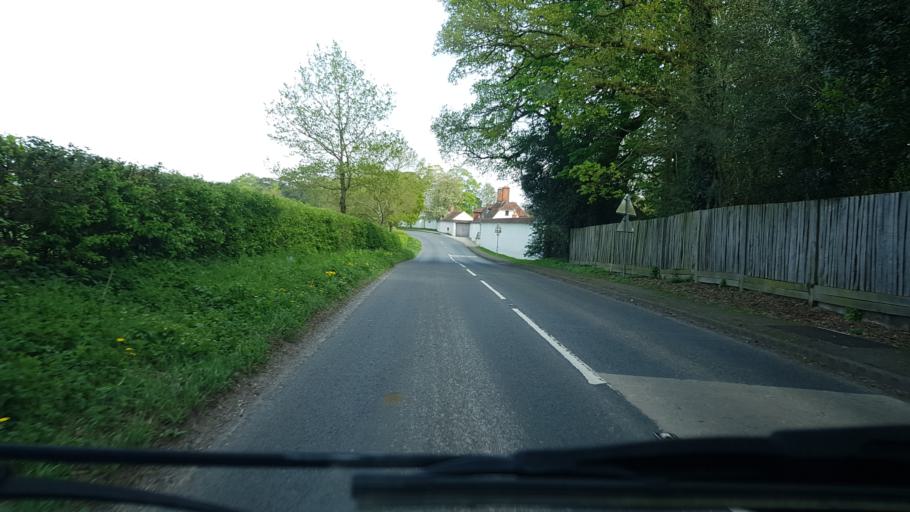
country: GB
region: England
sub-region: Hampshire
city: Overton
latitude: 51.2433
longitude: -1.2495
